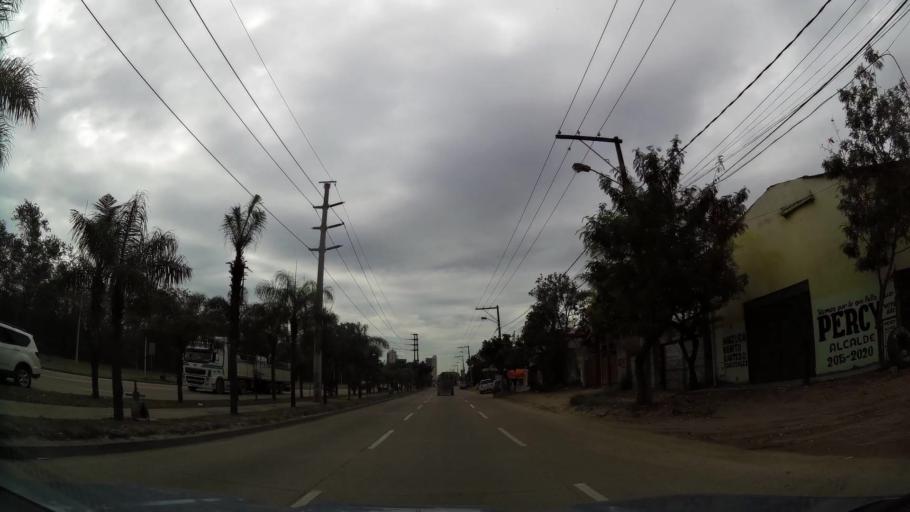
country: BO
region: Santa Cruz
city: Santa Cruz de la Sierra
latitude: -17.7695
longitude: -63.2089
